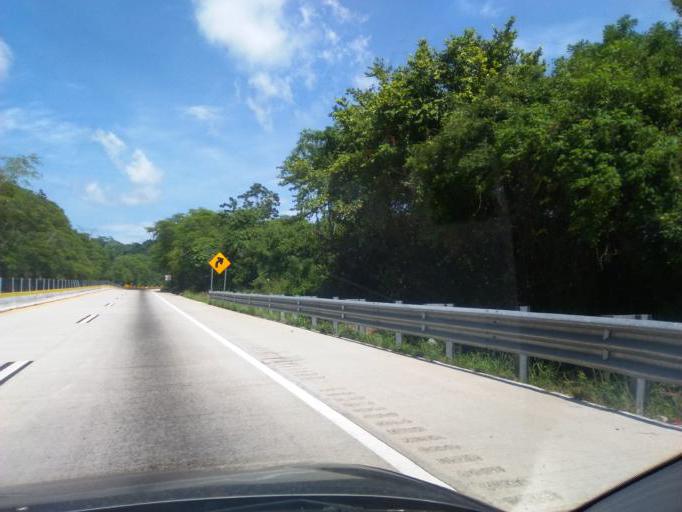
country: MX
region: Guerrero
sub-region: Acapulco de Juarez
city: Kilometro 30
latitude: 16.9468
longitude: -99.7648
